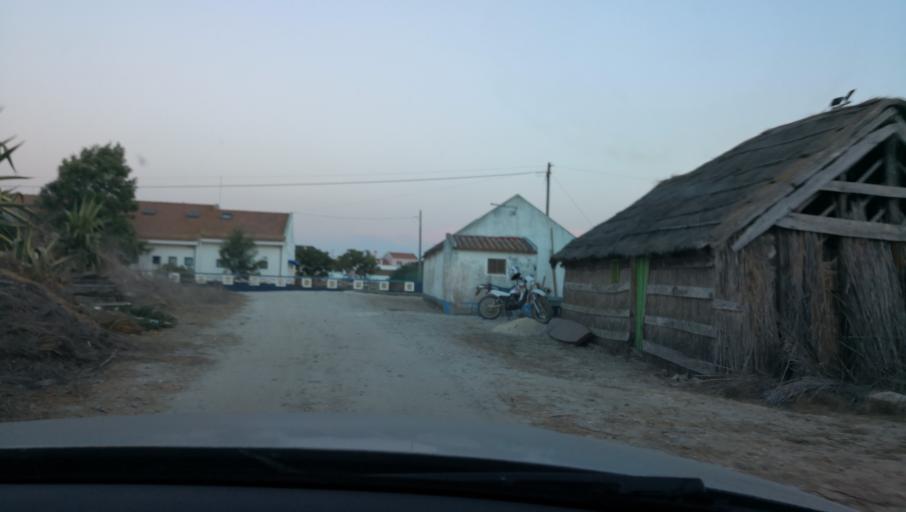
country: PT
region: Setubal
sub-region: Setubal
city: Setubal
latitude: 38.4093
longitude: -8.7545
